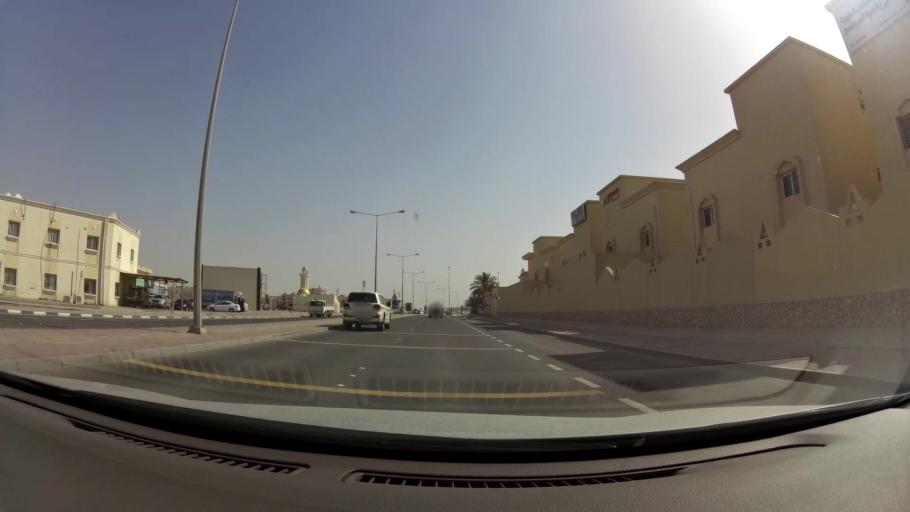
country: QA
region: Baladiyat ar Rayyan
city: Ar Rayyan
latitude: 25.3569
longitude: 51.4386
